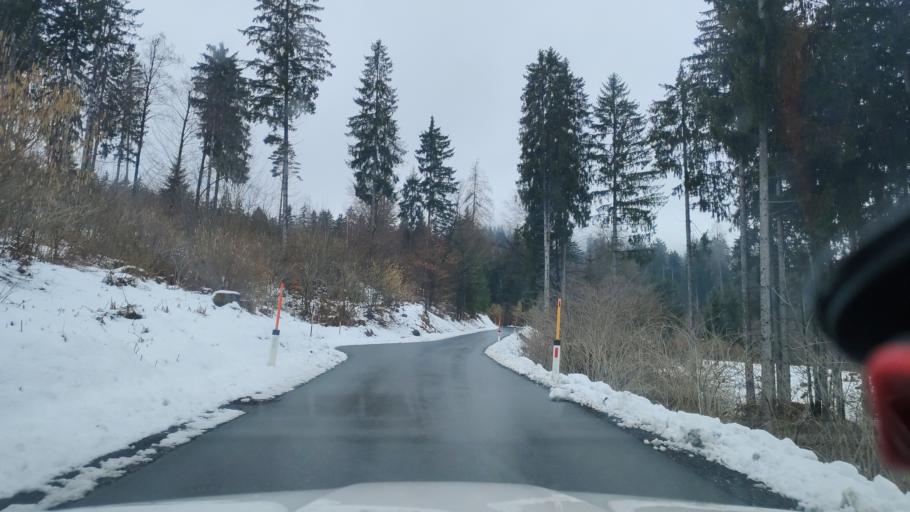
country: AT
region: Carinthia
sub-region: Politischer Bezirk Hermagor
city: Hermagor
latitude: 46.6264
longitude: 13.3557
